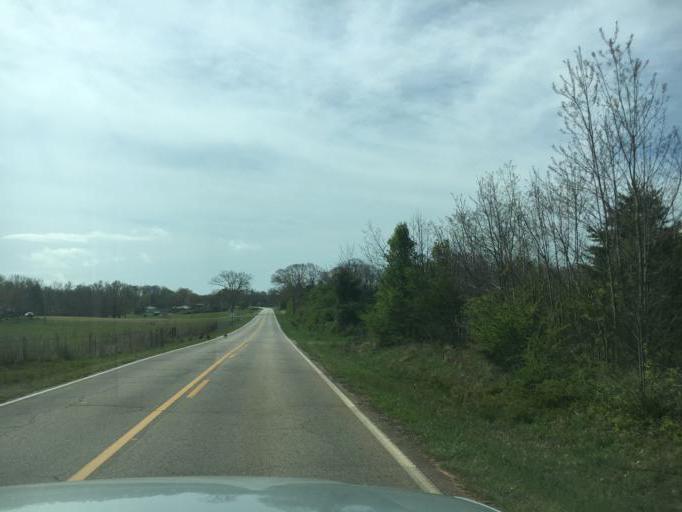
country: US
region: Georgia
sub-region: Franklin County
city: Lavonia
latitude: 34.3805
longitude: -83.0565
